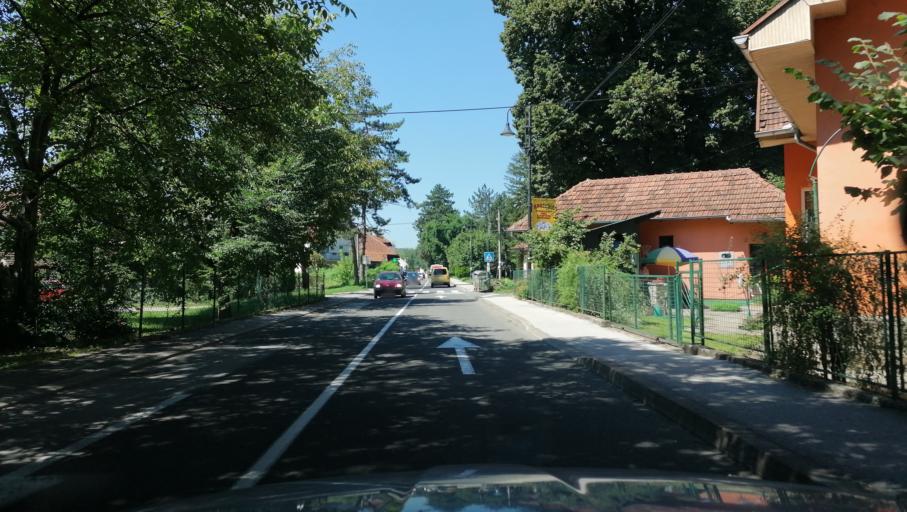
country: RS
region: Central Serbia
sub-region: Raski Okrug
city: Kraljevo
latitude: 43.6891
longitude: 20.6128
